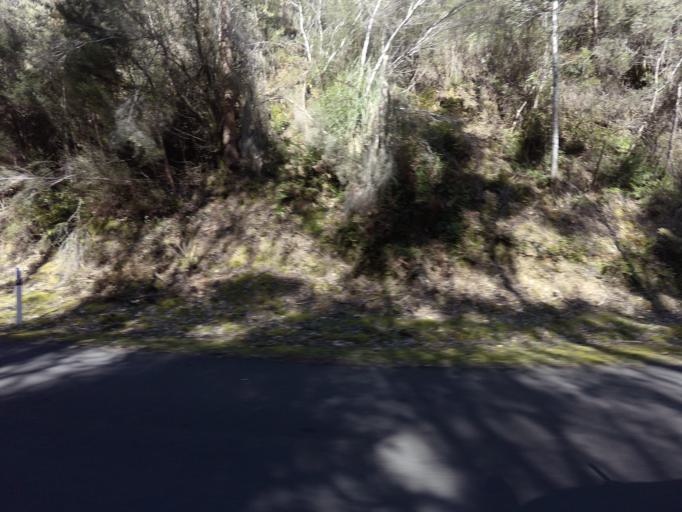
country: AU
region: Tasmania
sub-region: Derwent Valley
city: New Norfolk
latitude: -42.7280
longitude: 146.4292
